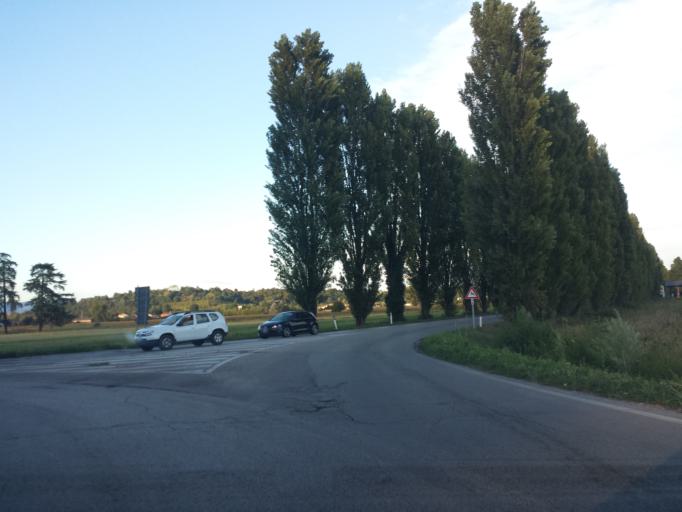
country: IT
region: Veneto
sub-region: Provincia di Vicenza
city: Creazzo
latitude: 45.5476
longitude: 11.4928
